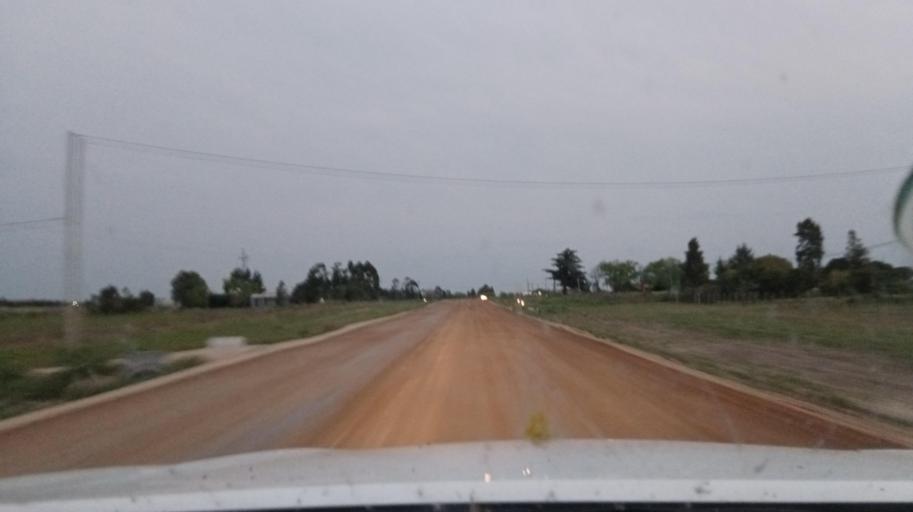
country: UY
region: Canelones
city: Santa Rosa
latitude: -34.5417
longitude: -56.1004
